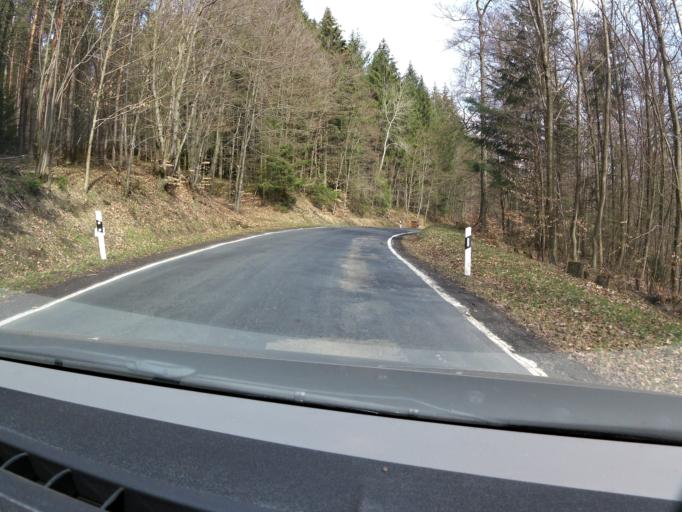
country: DE
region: Thuringia
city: Stadtlengsfeld
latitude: 50.7760
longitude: 10.1019
